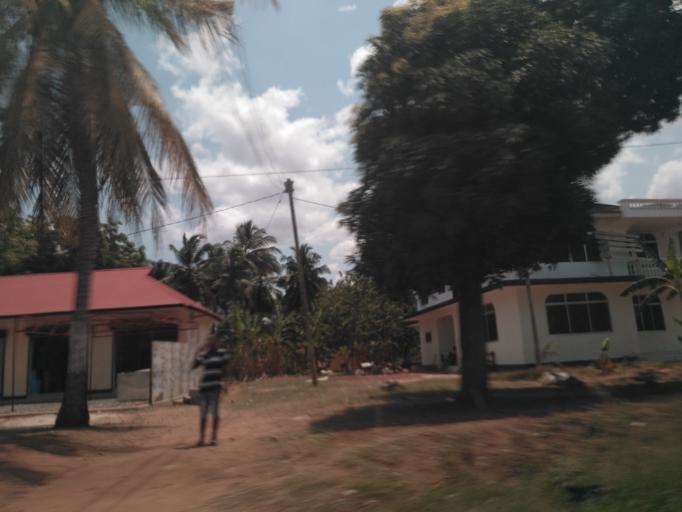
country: TZ
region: Dar es Salaam
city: Dar es Salaam
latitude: -6.8357
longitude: 39.3465
